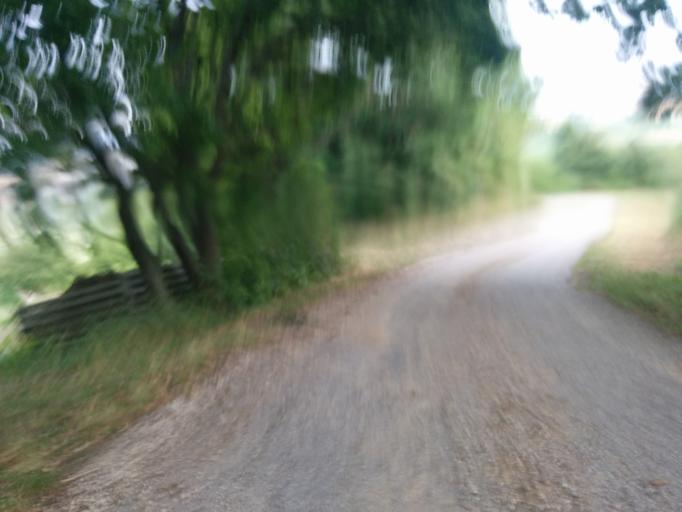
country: AT
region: Lower Austria
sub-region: Politischer Bezirk Modling
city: Gumpoldskirchen
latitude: 48.0404
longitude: 16.2593
